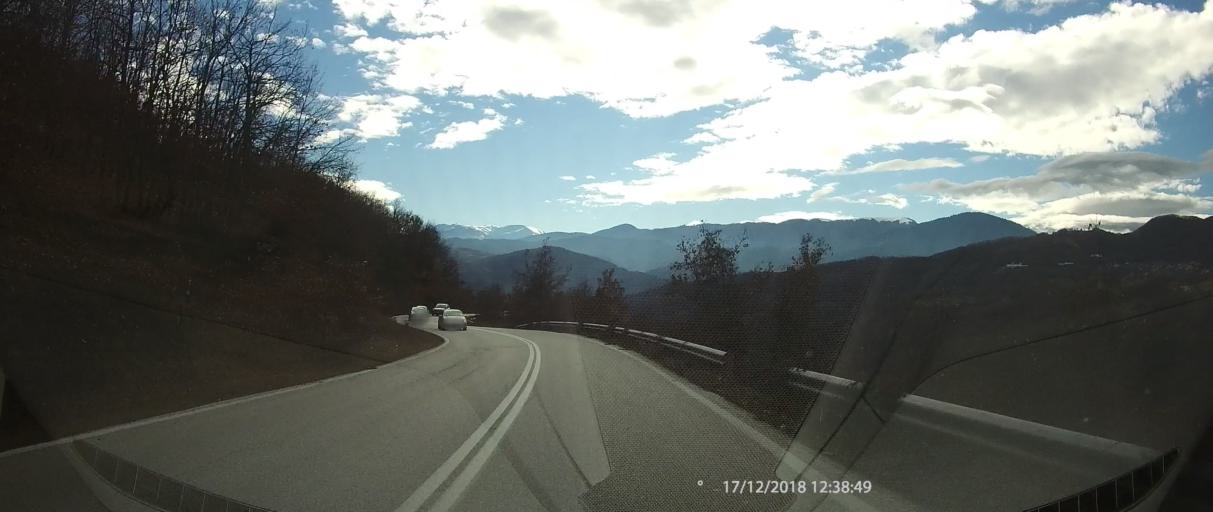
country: GR
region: Epirus
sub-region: Nomos Ioanninon
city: Metsovo
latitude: 39.8051
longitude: 21.3494
